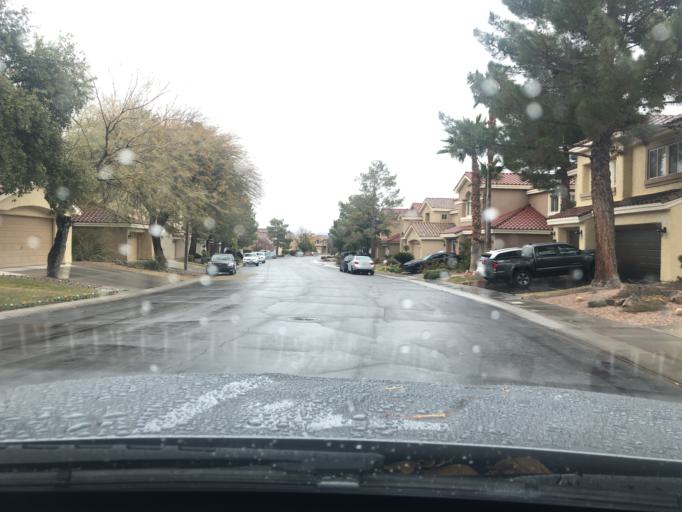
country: US
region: Nevada
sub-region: Clark County
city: Summerlin South
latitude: 36.1974
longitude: -115.2881
